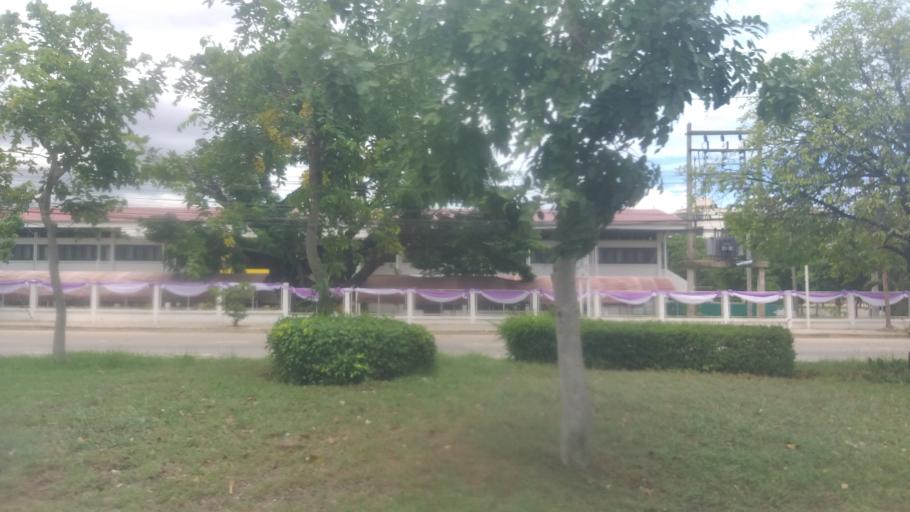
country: TH
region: Nakhon Ratchasima
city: Nakhon Ratchasima
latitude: 15.0332
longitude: 102.1375
